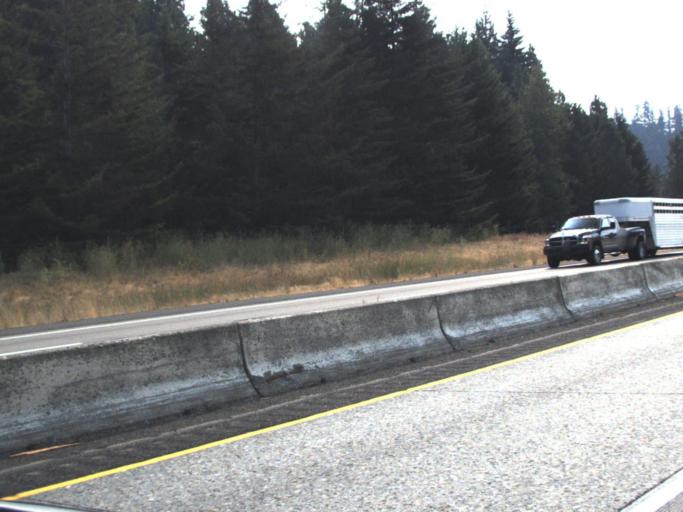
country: US
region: Washington
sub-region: Kittitas County
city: Cle Elum
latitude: 47.1905
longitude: -121.0467
